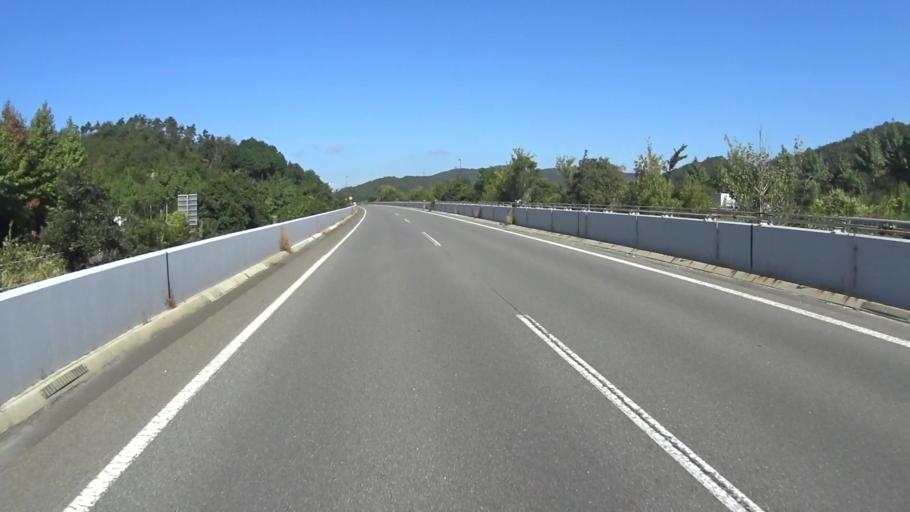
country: JP
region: Kyoto
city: Kameoka
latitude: 35.0789
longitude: 135.5138
